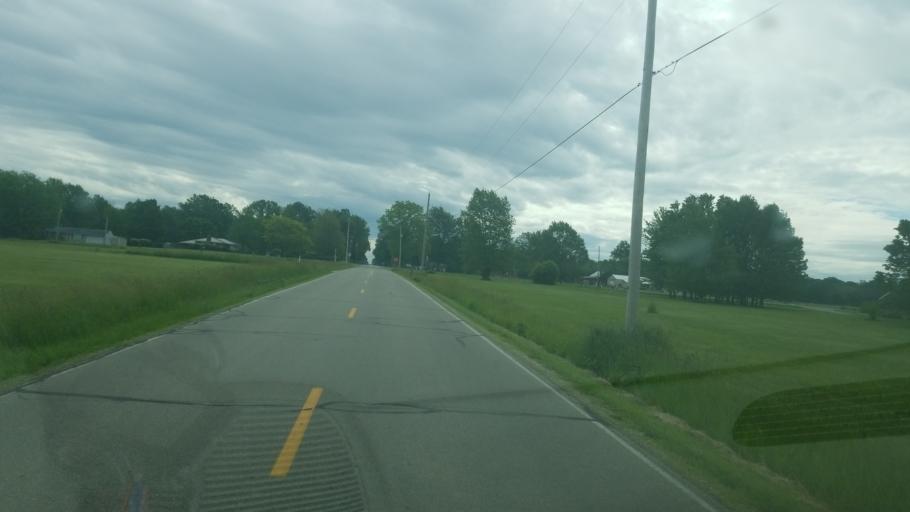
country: US
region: Ohio
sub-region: Crawford County
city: Crestline
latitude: 40.8286
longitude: -82.7915
